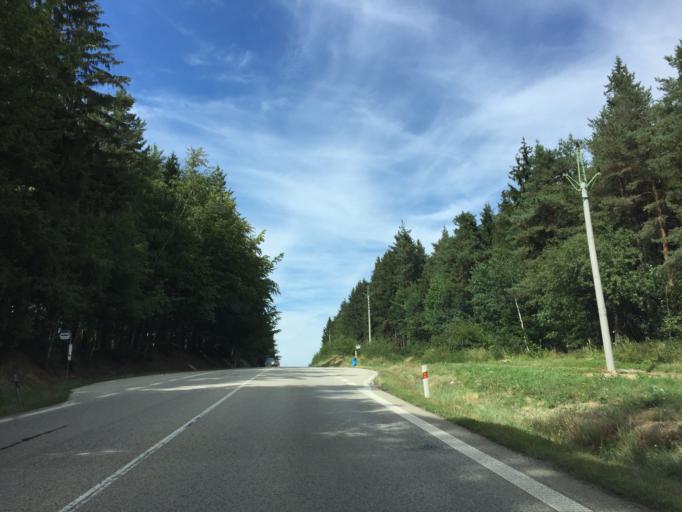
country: CZ
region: Central Bohemia
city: Votice
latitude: 49.5894
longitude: 14.6614
